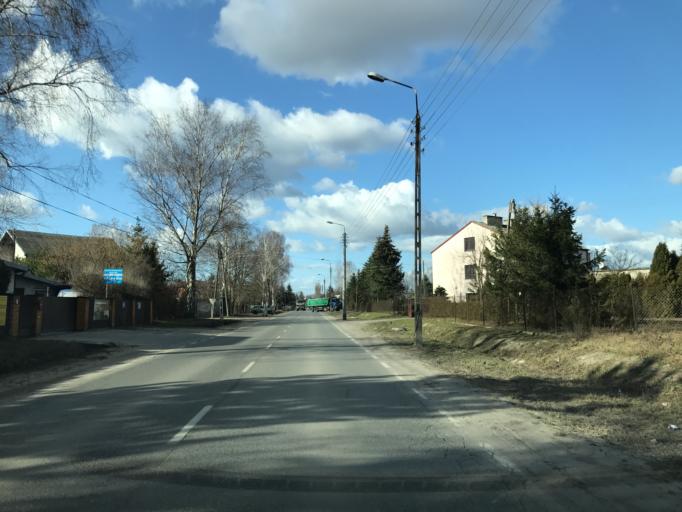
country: PL
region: Masovian Voivodeship
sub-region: Powiat wolominski
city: Radzymin
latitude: 52.4075
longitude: 21.1921
